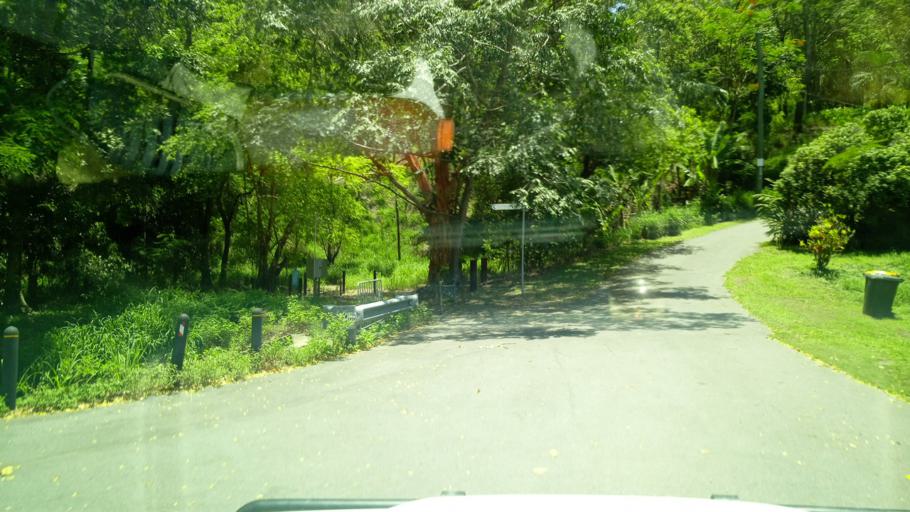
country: AU
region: Queensland
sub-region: Cairns
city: Cairns
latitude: -16.8886
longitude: 145.7479
